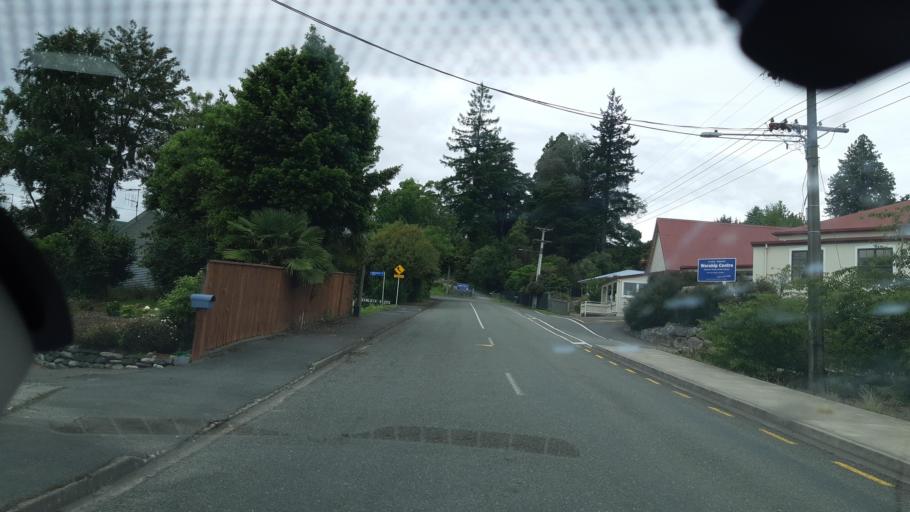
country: NZ
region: Tasman
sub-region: Tasman District
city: Wakefield
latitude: -41.4087
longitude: 173.0461
